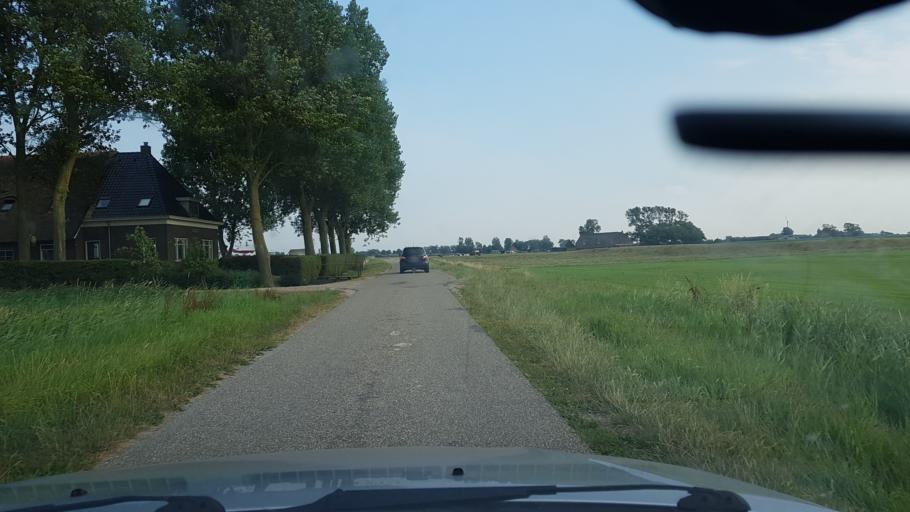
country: NL
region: Friesland
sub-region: Gemeente Dongeradeel
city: Holwerd
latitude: 53.3394
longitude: 5.8685
